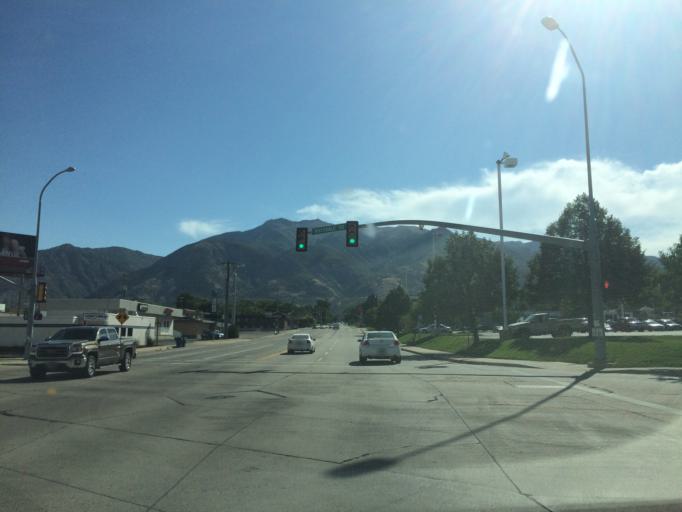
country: US
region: Utah
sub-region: Weber County
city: South Ogden
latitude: 41.1978
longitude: -111.9740
